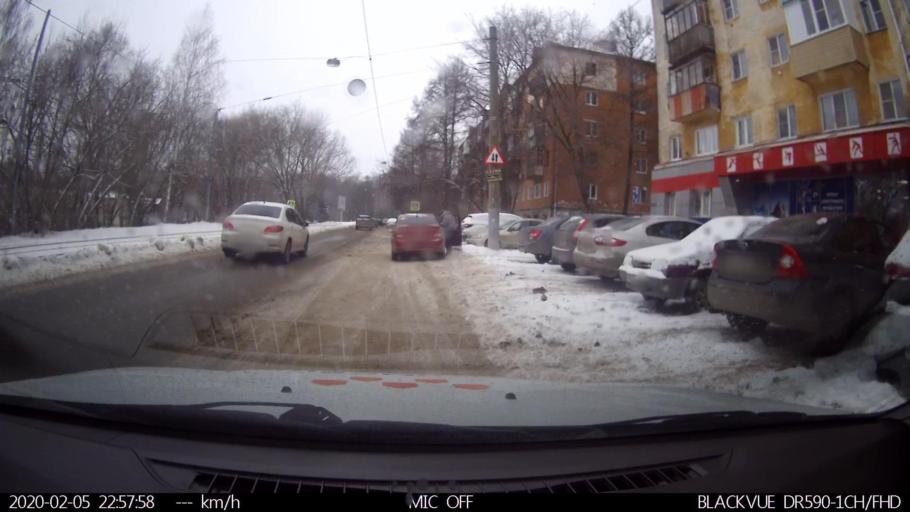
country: RU
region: Penza
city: Bogoslovka
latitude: 53.2502
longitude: 44.8469
